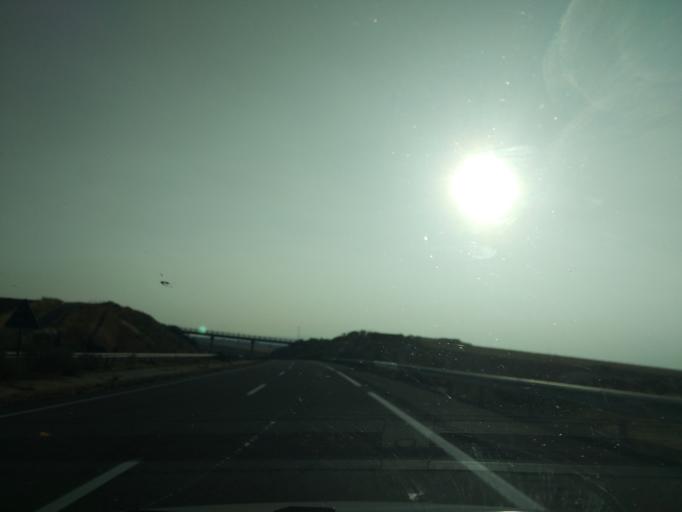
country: ES
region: Castille and Leon
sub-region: Provincia de Avila
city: Ojos-Albos
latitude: 40.7507
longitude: -4.4753
